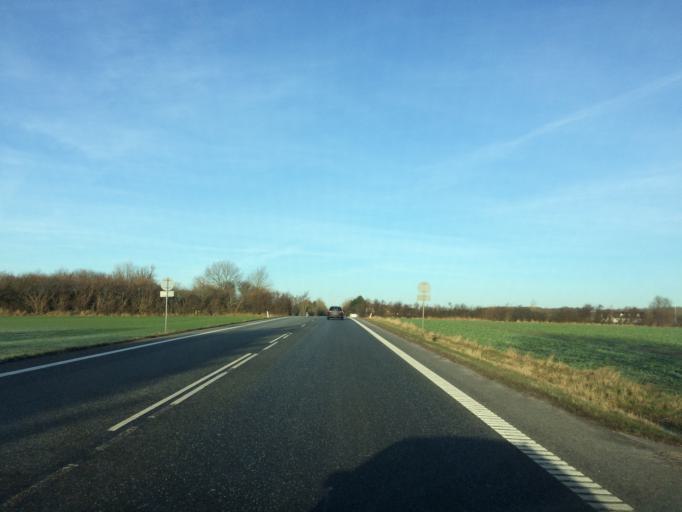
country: DK
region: South Denmark
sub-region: Fredericia Kommune
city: Snoghoj
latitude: 55.5481
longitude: 9.6798
